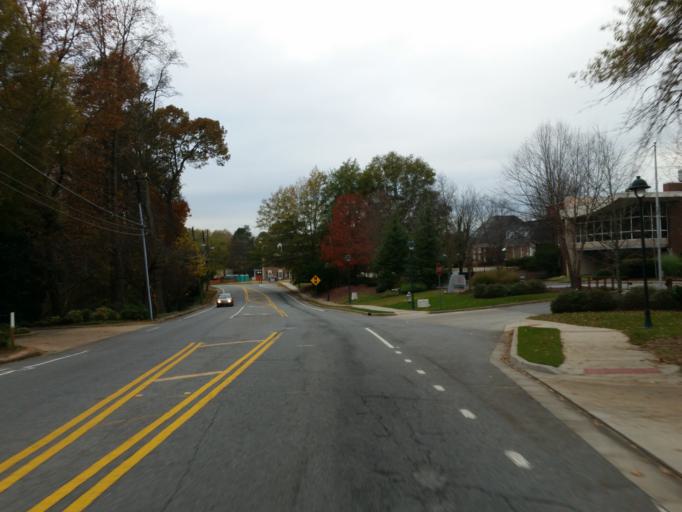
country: US
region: Georgia
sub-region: Fulton County
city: Sandy Springs
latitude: 33.9027
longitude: -84.3752
